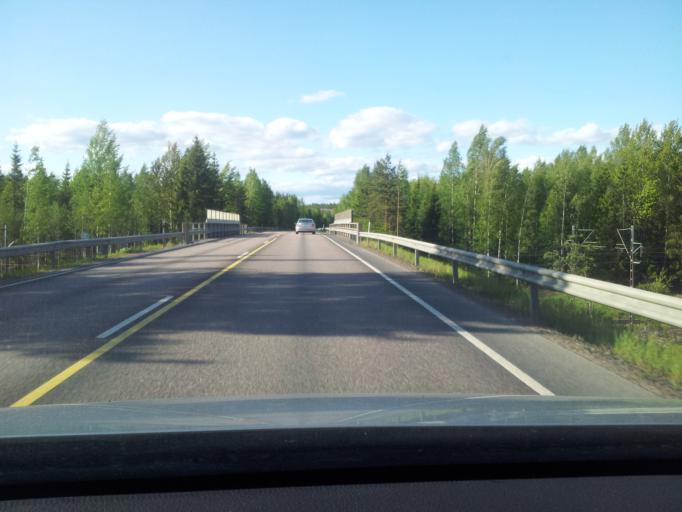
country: FI
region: Kymenlaakso
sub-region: Kouvola
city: Elimaeki
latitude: 60.8457
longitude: 26.5427
